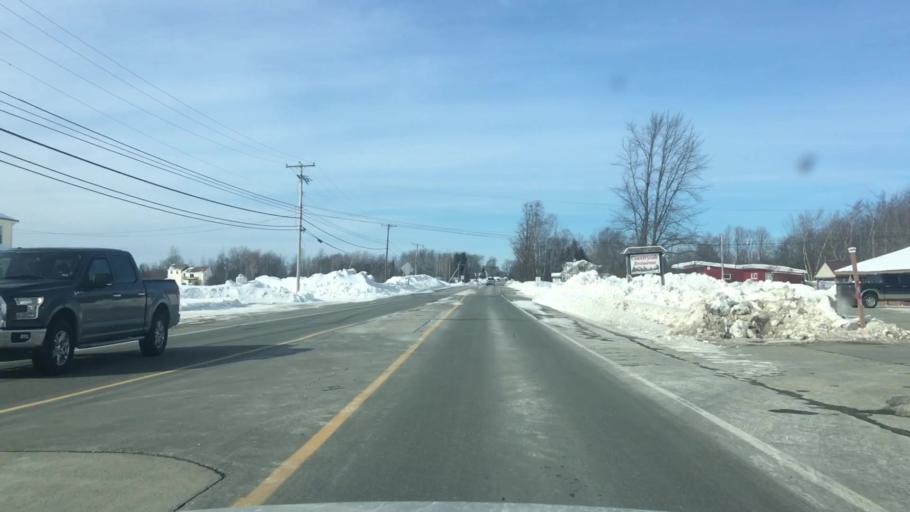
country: US
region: Maine
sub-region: Penobscot County
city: Charleston
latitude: 45.0175
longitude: -69.0281
